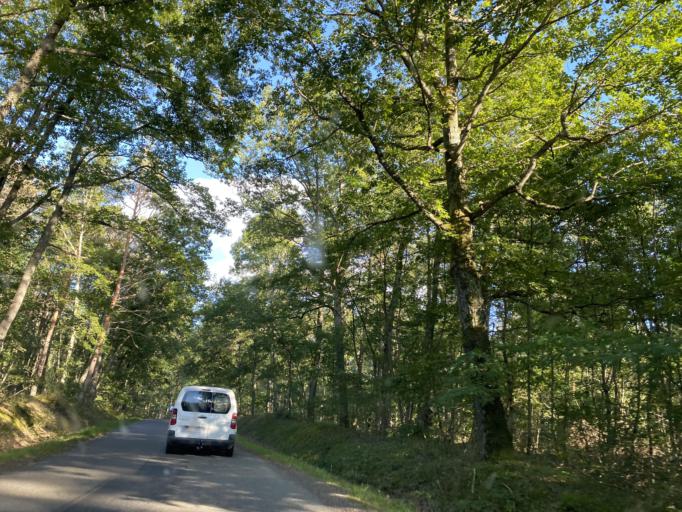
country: FR
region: Auvergne
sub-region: Departement du Puy-de-Dome
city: Randan
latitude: 46.0346
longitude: 3.3331
